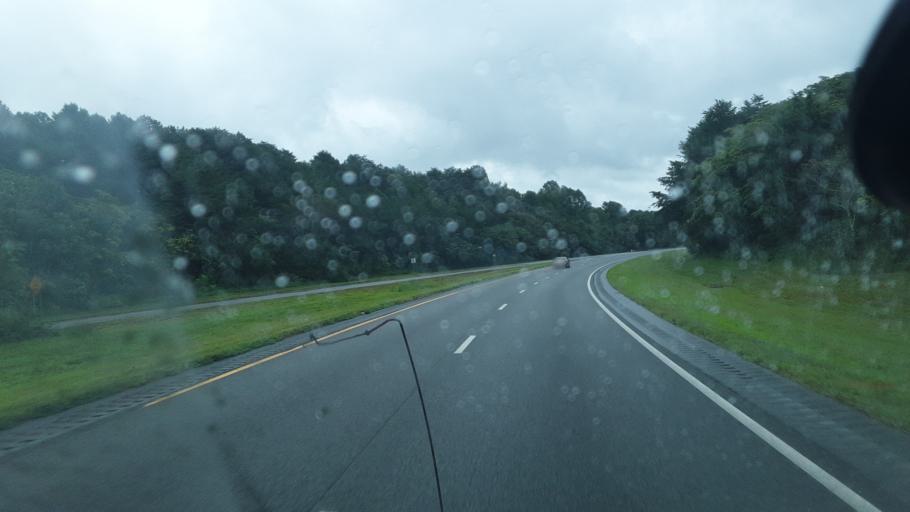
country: US
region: North Carolina
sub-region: Davidson County
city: Wallburg
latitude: 36.0610
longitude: -80.1841
